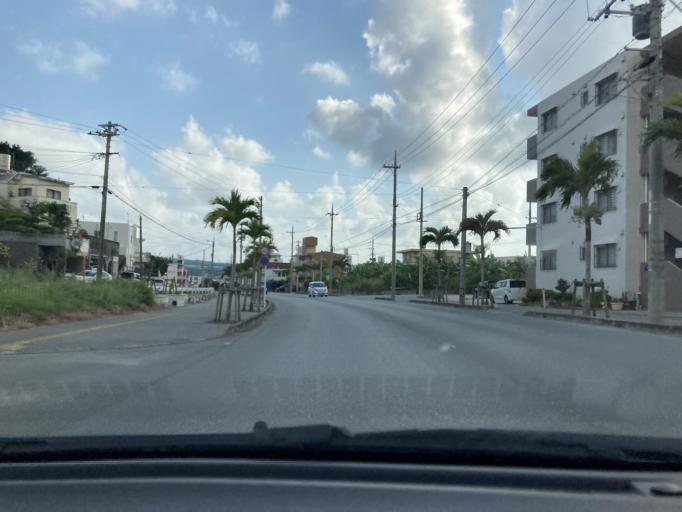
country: JP
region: Okinawa
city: Tomigusuku
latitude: 26.1542
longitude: 127.7177
